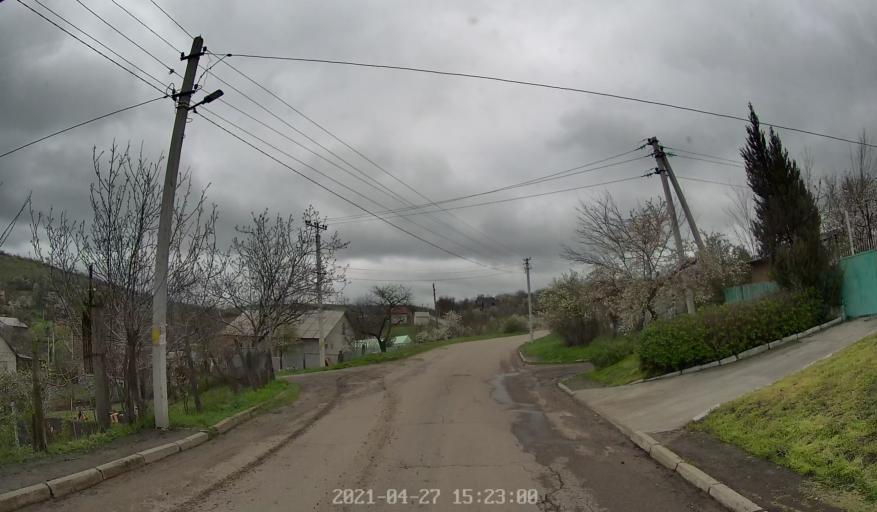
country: MD
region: Chisinau
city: Vadul lui Voda
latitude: 47.0252
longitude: 29.0248
